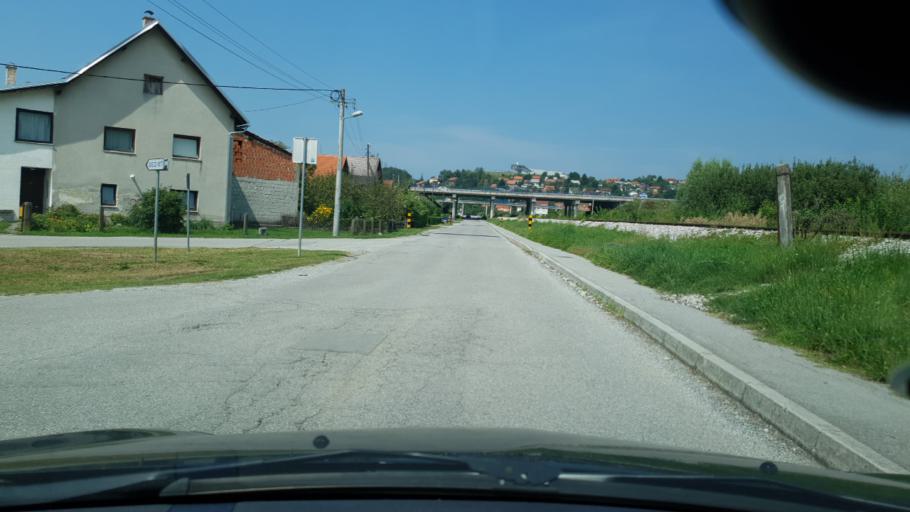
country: HR
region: Krapinsko-Zagorska
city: Zabok
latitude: 46.0244
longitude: 15.9166
